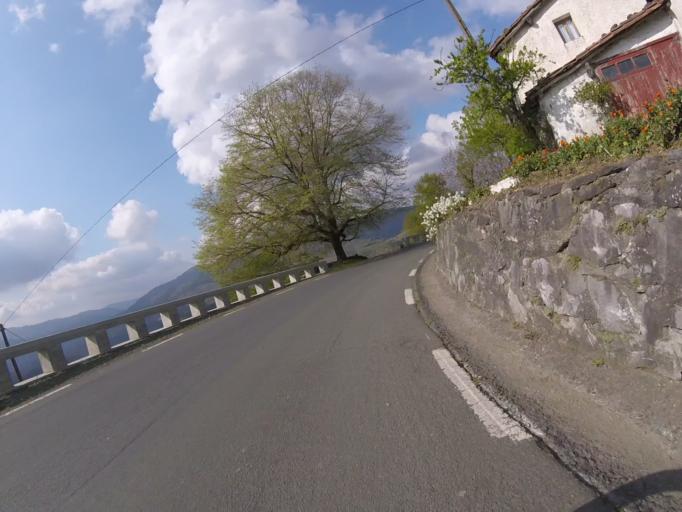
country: ES
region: Basque Country
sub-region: Provincia de Guipuzcoa
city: Azkoitia
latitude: 43.2059
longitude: -2.3500
